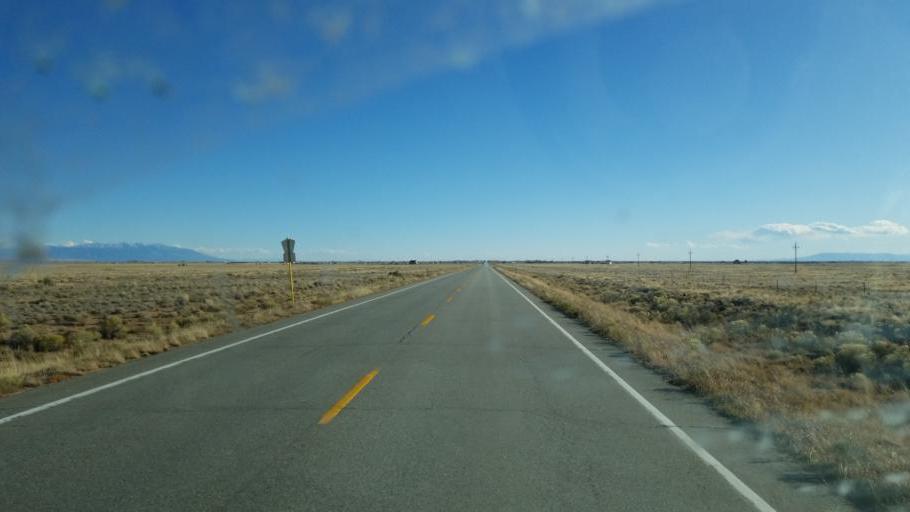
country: US
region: Colorado
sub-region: Saguache County
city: Saguache
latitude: 38.1617
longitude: -105.9266
